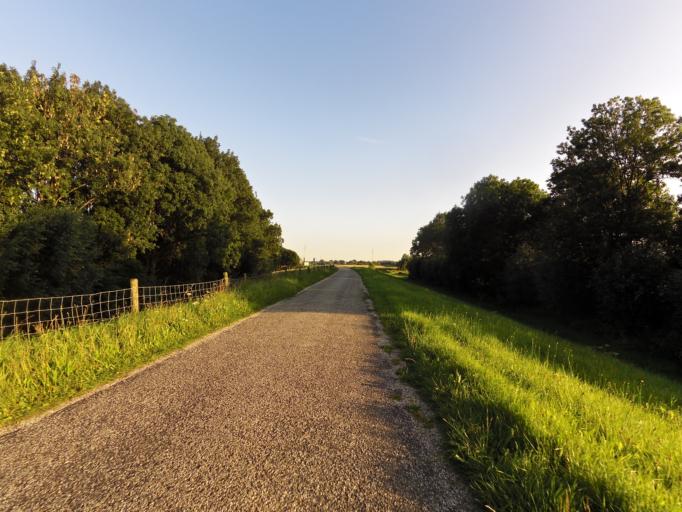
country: NL
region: Gelderland
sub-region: Gemeente Duiven
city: Duiven
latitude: 51.9154
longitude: 5.9968
